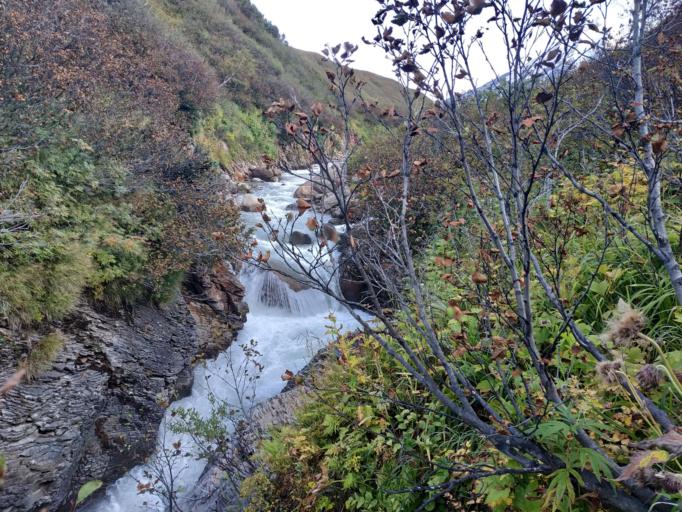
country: RU
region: Kamtsjatka
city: Petropavlovsk-Kamchatsky
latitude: 53.4228
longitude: 158.7398
